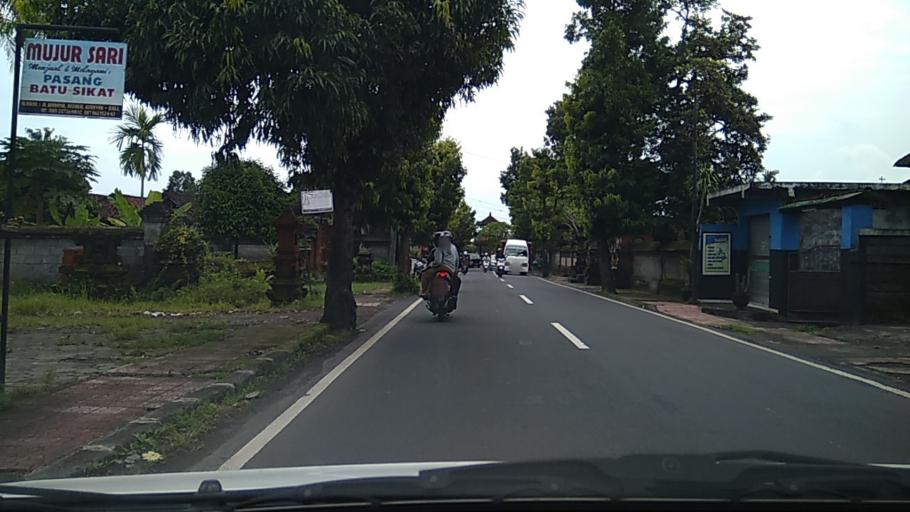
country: ID
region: Bali
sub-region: Kabupaten Gianyar
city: Ubud
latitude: -8.5288
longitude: 115.2965
